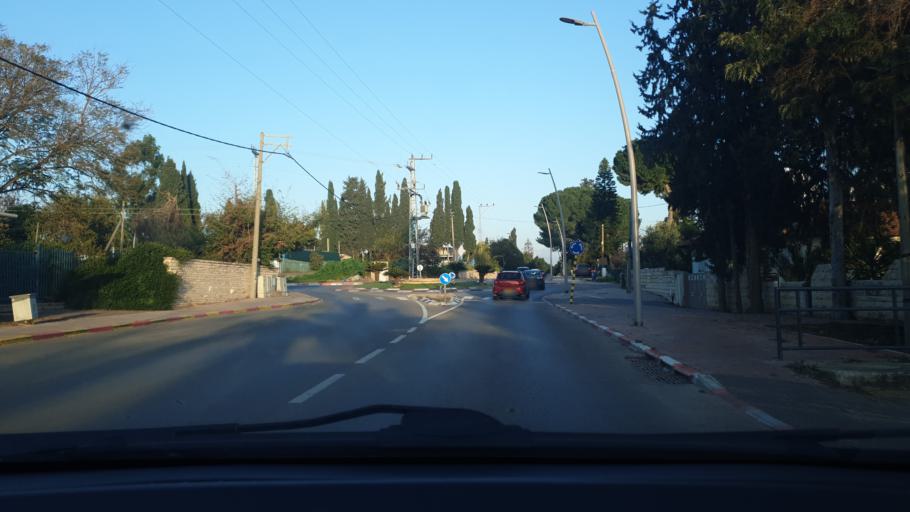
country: IL
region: Central District
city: Ramla
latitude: 31.9359
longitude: 34.8443
